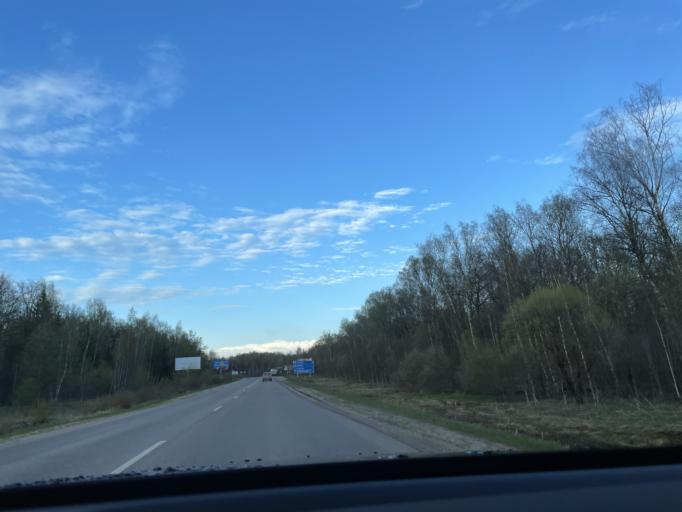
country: RU
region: Tula
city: Aleksin
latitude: 54.5130
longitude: 37.1338
